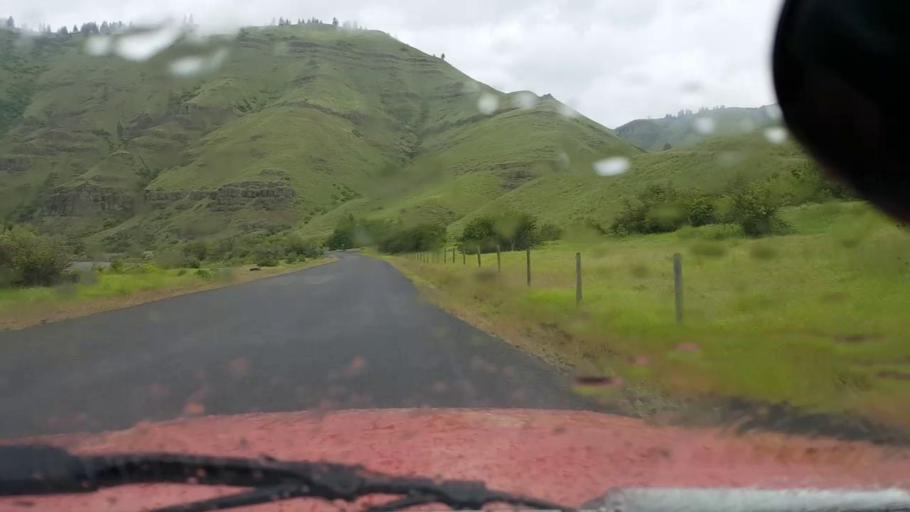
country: US
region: Washington
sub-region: Asotin County
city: Asotin
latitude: 46.0309
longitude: -117.3169
